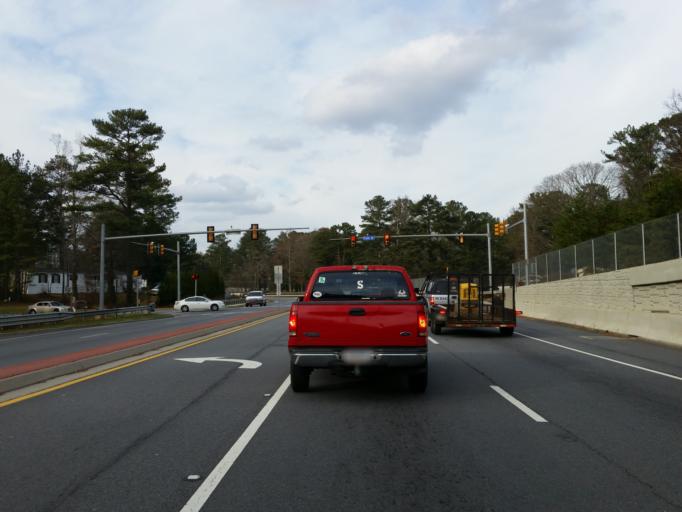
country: US
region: Georgia
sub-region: Cobb County
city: Fair Oaks
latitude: 33.9019
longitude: -84.5994
